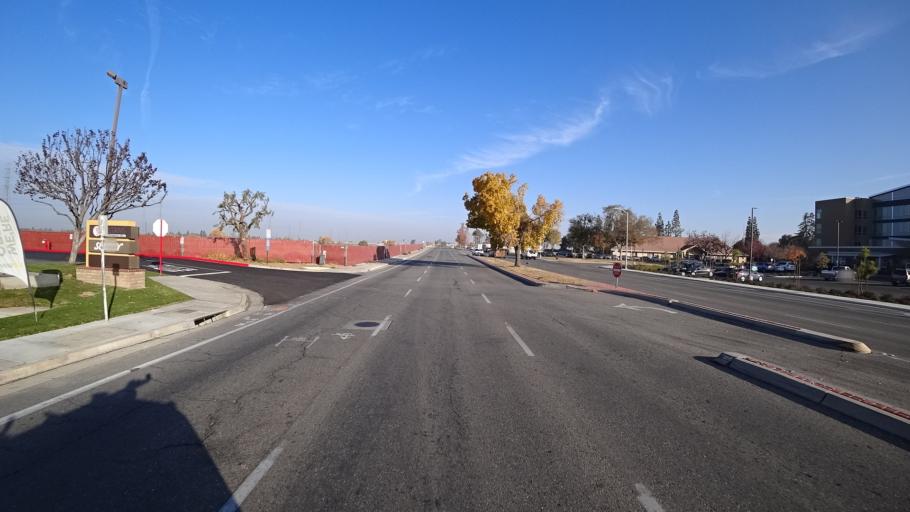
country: US
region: California
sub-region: Kern County
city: Greenacres
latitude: 35.3574
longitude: -119.0923
